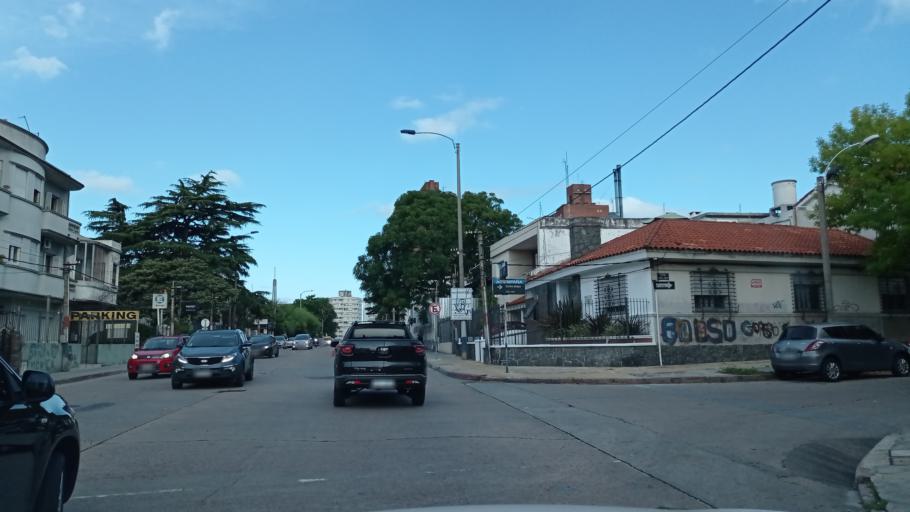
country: UY
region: Montevideo
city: Montevideo
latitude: -34.8872
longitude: -56.1627
